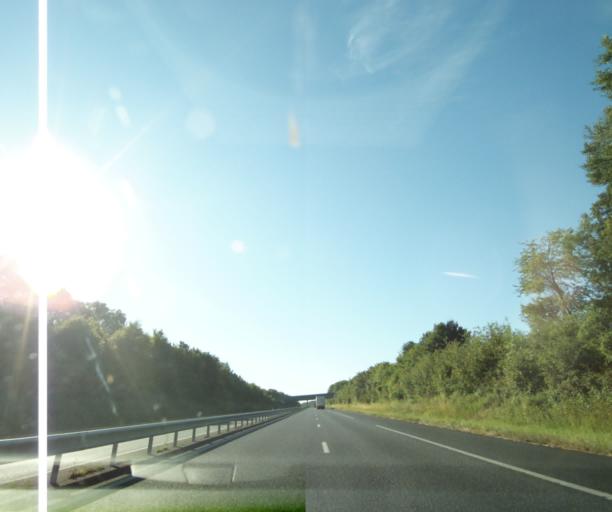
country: FR
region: Bourgogne
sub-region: Departement de l'Yonne
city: Soucy
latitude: 48.2400
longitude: 3.3691
